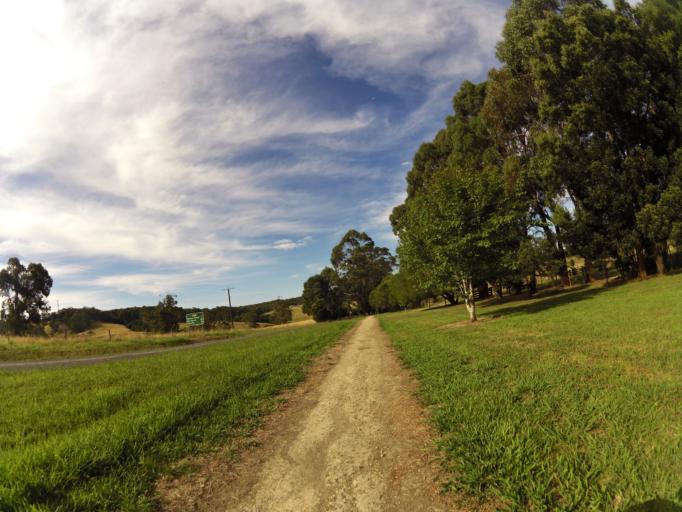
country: AU
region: Victoria
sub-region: Colac-Otway
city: Colac
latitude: -38.5117
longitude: 143.7167
